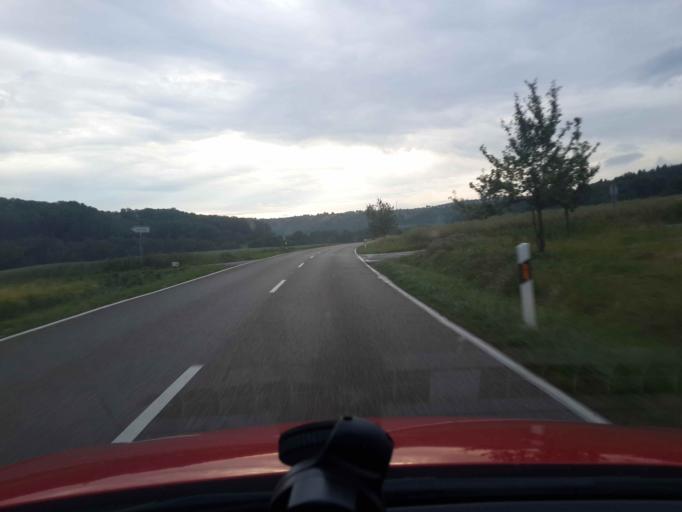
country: DE
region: Baden-Wuerttemberg
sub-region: Regierungsbezirk Stuttgart
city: Neudenau
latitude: 49.2717
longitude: 9.2458
